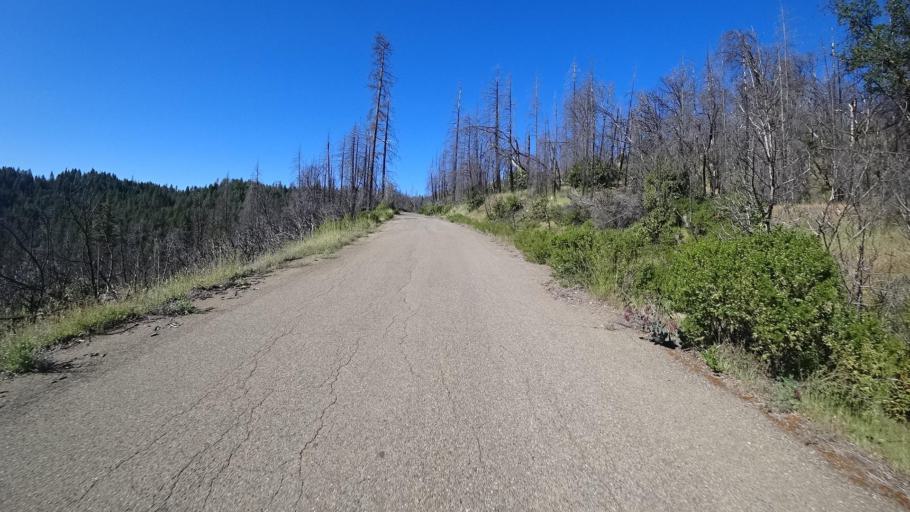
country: US
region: California
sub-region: Lake County
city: Upper Lake
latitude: 39.3976
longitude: -122.9606
